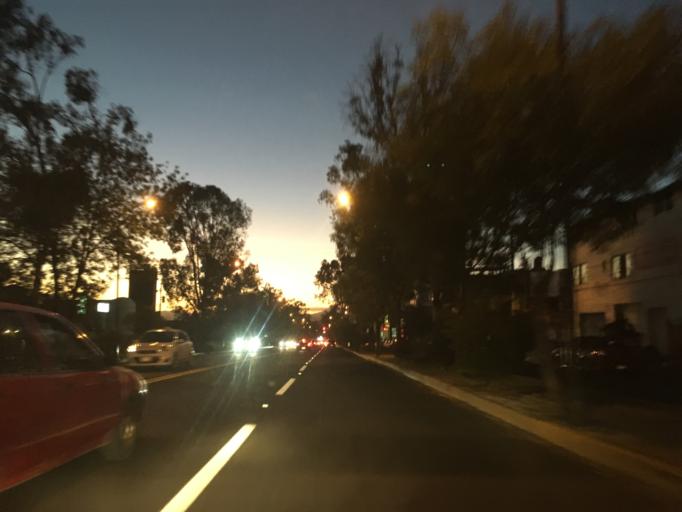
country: MX
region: Michoacan
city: Morelia
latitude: 19.6953
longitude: -101.1563
